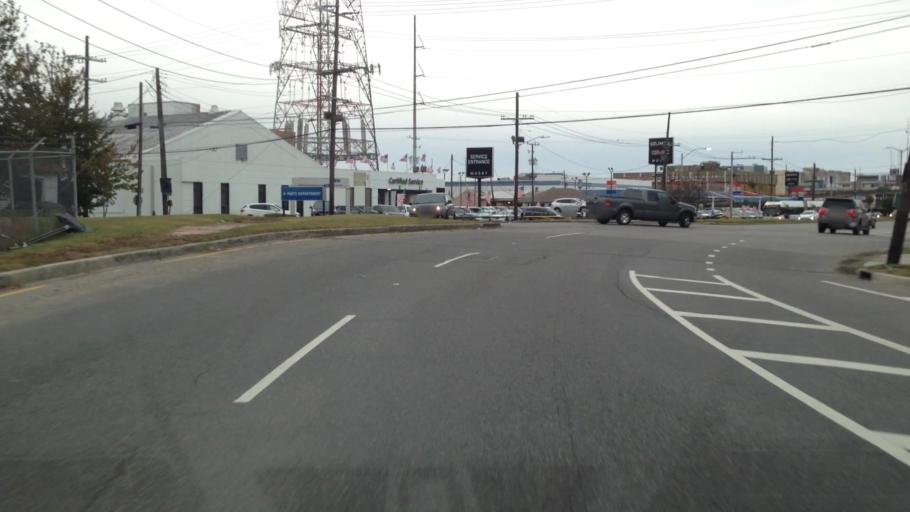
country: US
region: Louisiana
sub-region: Orleans Parish
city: New Orleans
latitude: 29.9523
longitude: -90.0980
